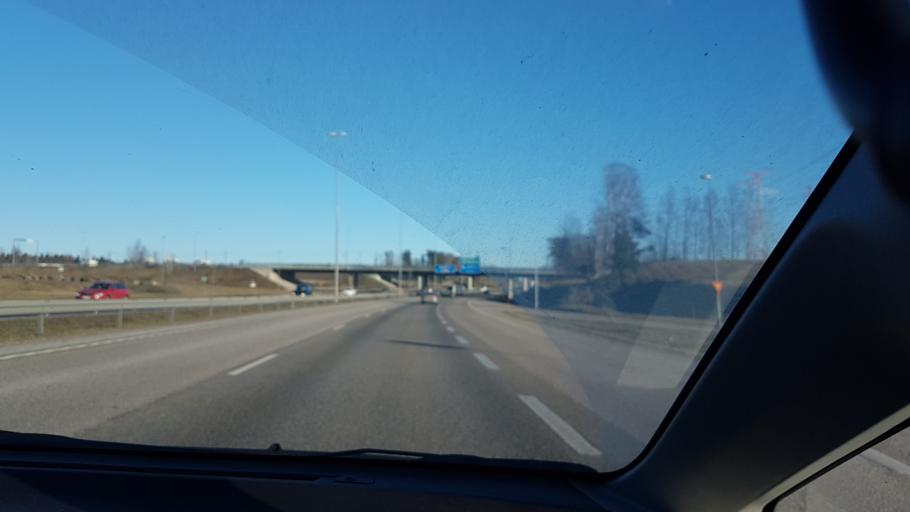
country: FI
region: Uusimaa
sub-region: Helsinki
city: Kilo
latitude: 60.2909
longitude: 24.8390
